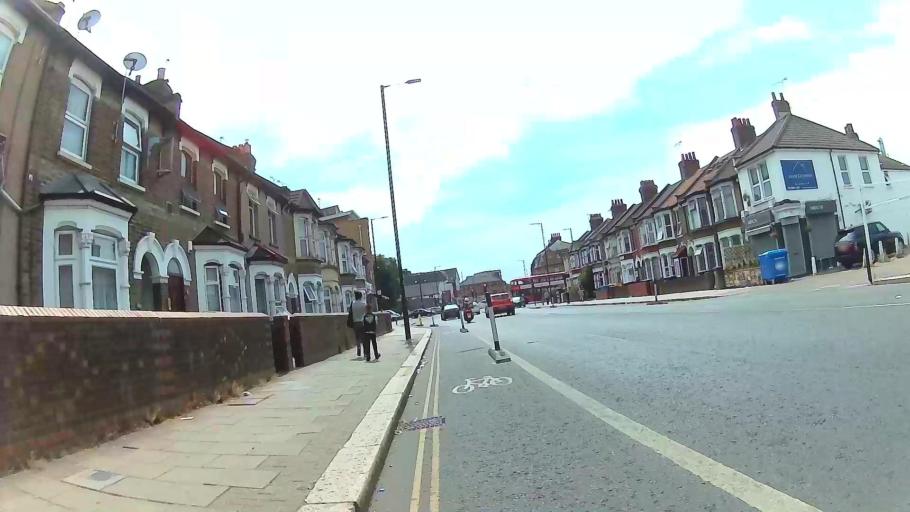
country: GB
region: England
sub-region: Greater London
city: Enfield
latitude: 51.6492
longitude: -0.0462
